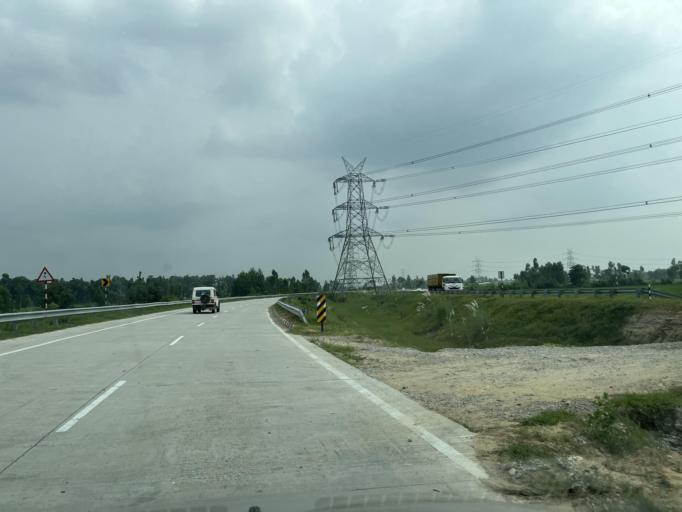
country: IN
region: Uttarakhand
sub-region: Udham Singh Nagar
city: Jaspur
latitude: 29.2790
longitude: 78.8674
